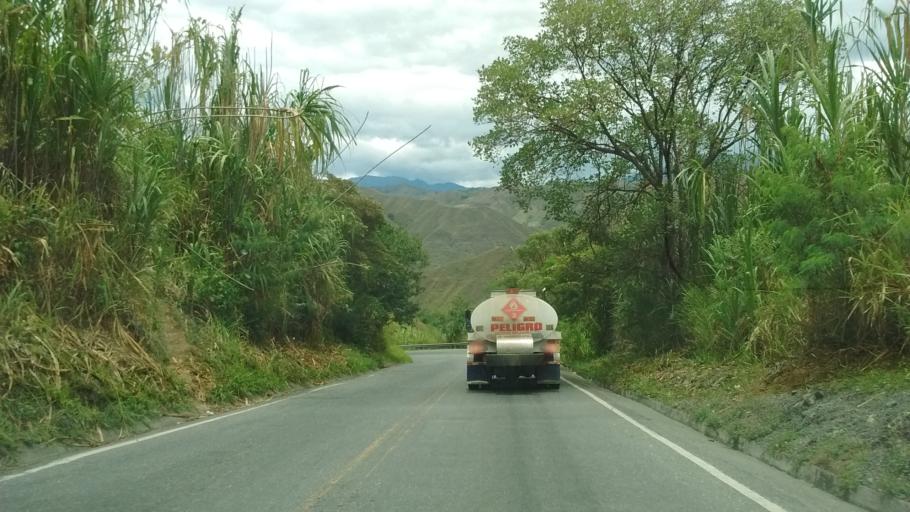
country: CO
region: Cauca
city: La Sierra
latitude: 2.2000
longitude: -76.8273
